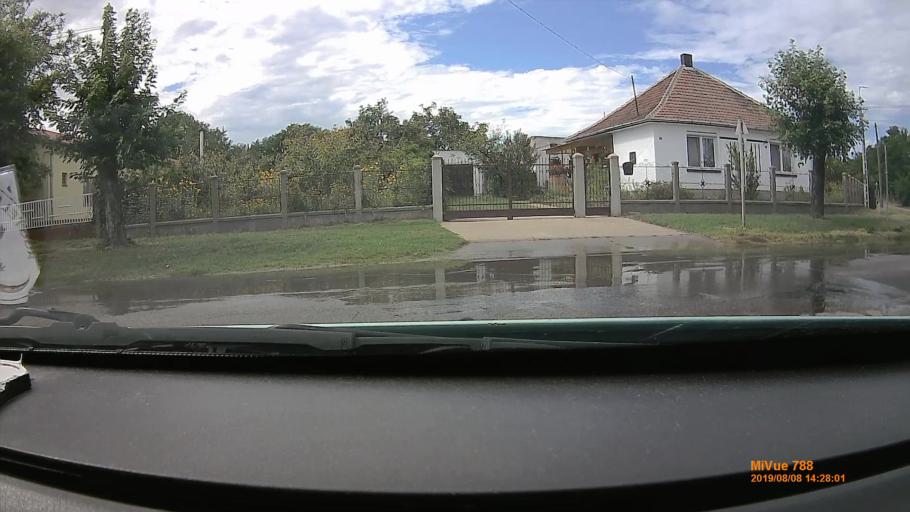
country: HU
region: Szabolcs-Szatmar-Bereg
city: Mateszalka
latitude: 47.9477
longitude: 22.3210
